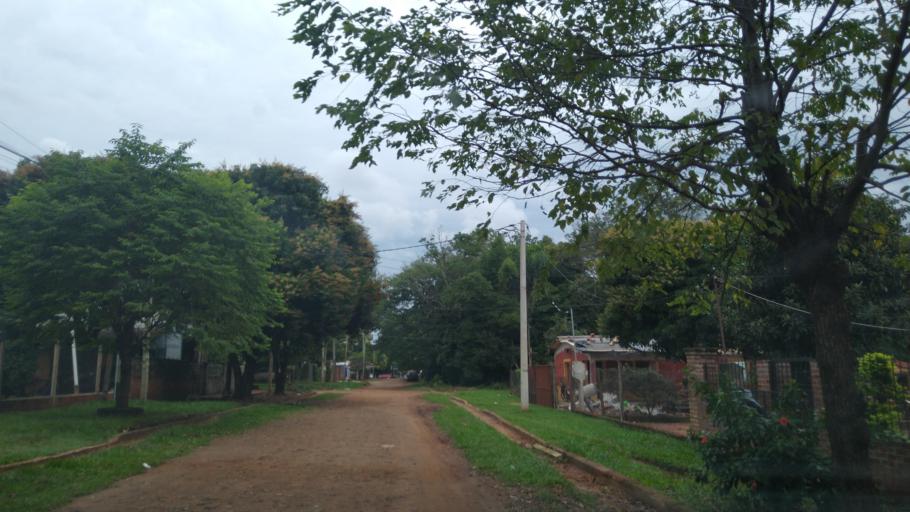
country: AR
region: Misiones
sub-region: Departamento de Capital
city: Posadas
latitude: -27.3725
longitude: -55.9271
